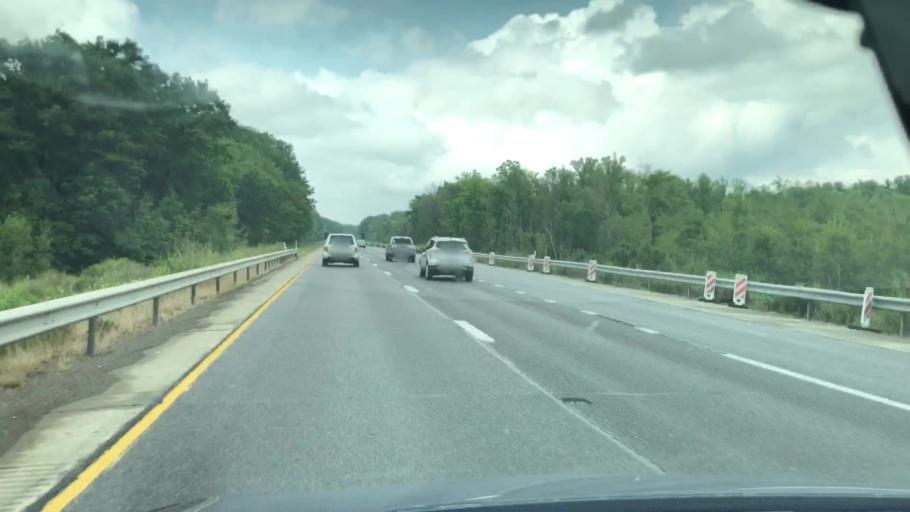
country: US
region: Pennsylvania
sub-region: Erie County
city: Fairview
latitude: 42.0013
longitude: -80.1621
